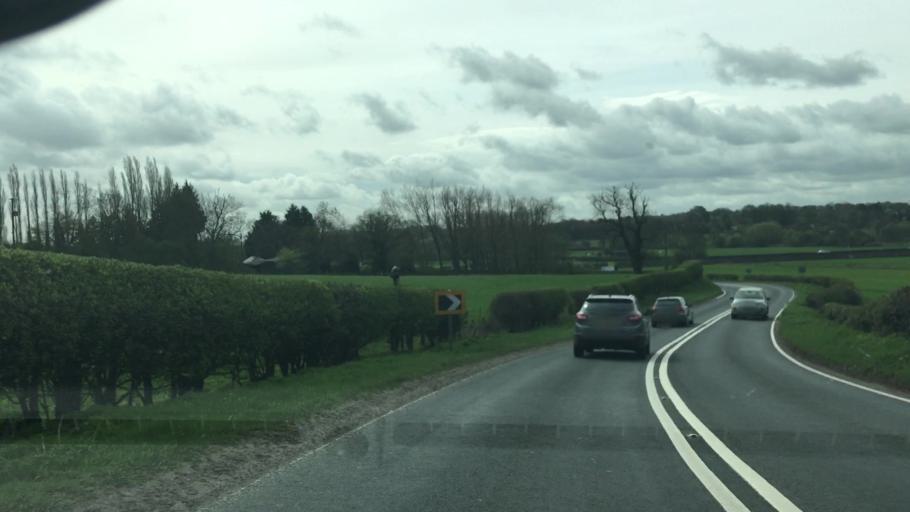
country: GB
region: England
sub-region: City and Borough of Leeds
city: Collingham
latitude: 53.9586
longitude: -1.4418
